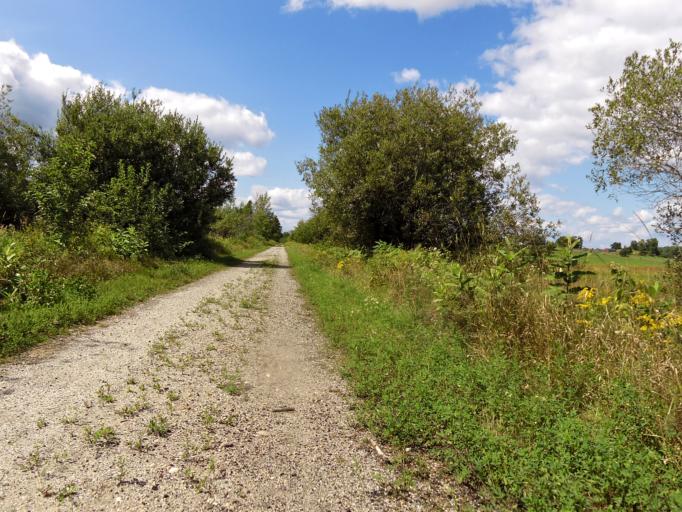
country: CA
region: Quebec
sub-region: Outaouais
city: Wakefield
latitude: 45.8648
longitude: -76.0127
